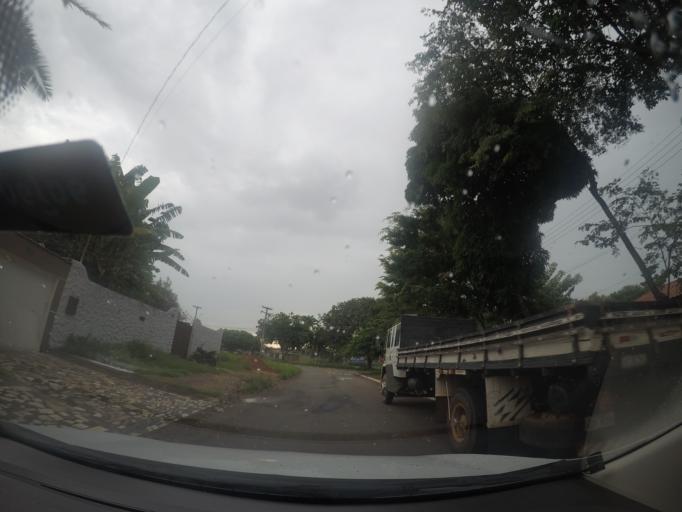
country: BR
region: Goias
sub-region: Goiania
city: Goiania
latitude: -16.6425
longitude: -49.2347
